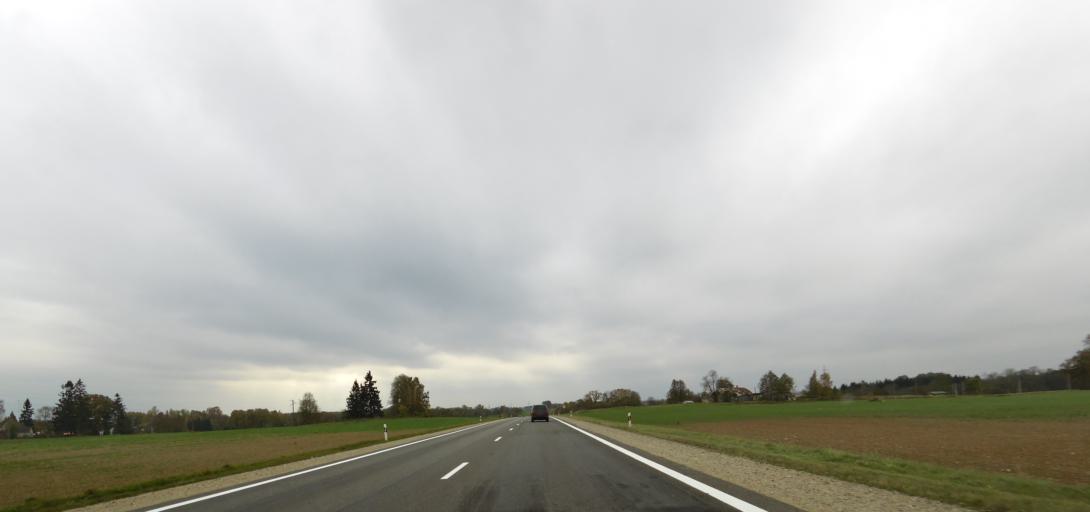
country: LT
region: Panevezys
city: Pasvalys
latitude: 56.0914
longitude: 24.4496
